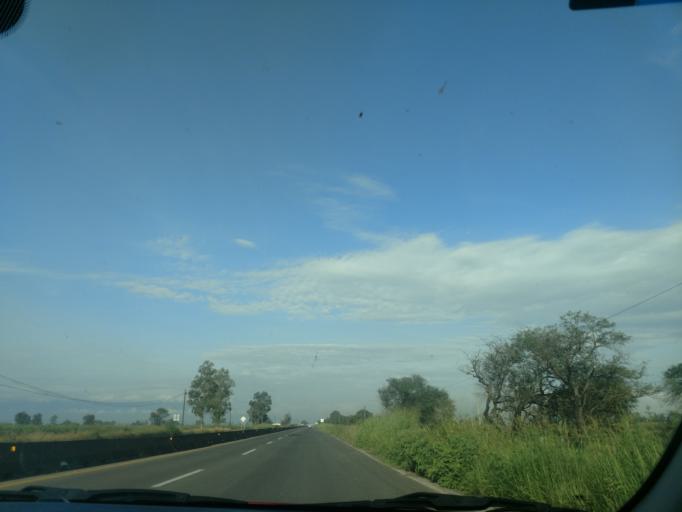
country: MX
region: Jalisco
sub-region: Ameca
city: Los Pocitos
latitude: 20.5361
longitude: -103.9472
